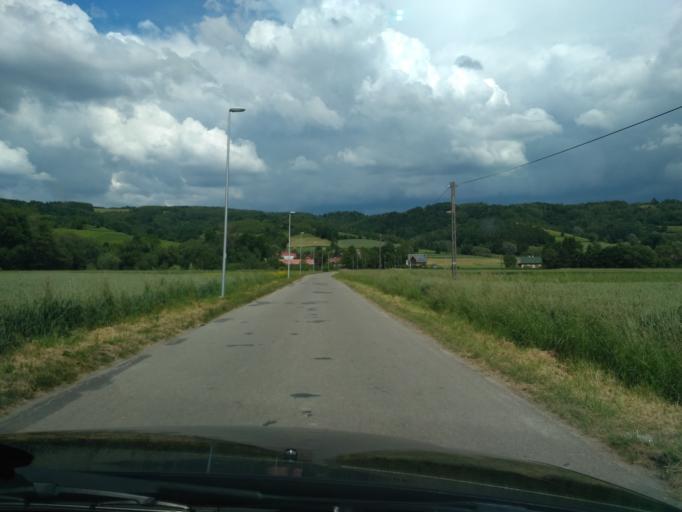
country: PL
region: Subcarpathian Voivodeship
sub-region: Powiat strzyzowski
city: Strzyzow
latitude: 49.8352
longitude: 21.8299
